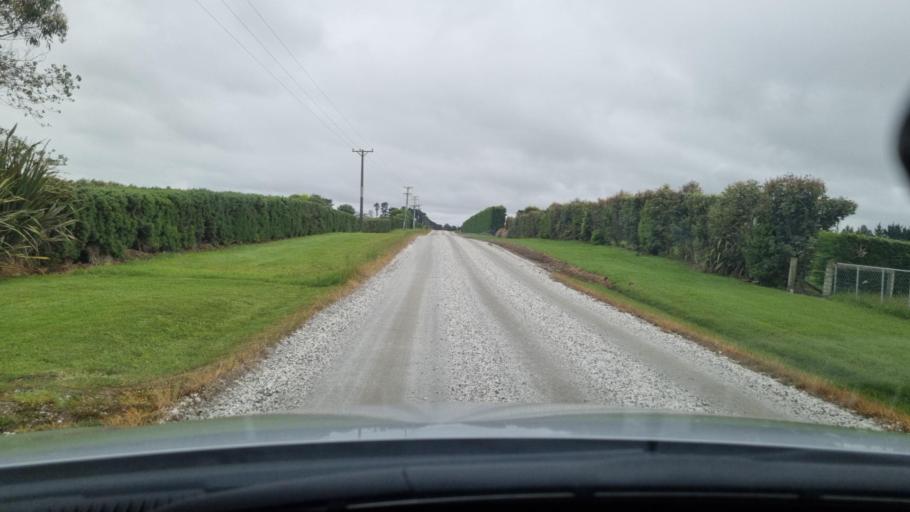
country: NZ
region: Southland
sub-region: Invercargill City
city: Invercargill
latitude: -46.4130
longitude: 168.4412
